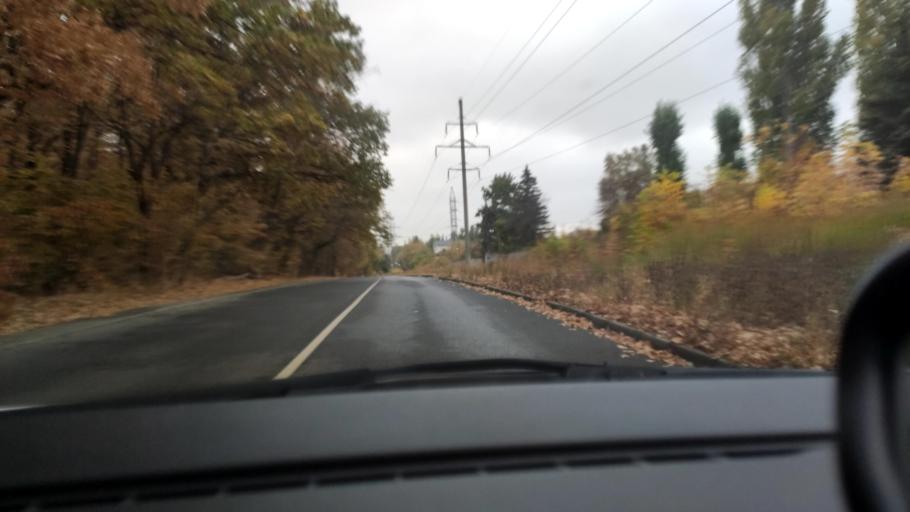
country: RU
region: Voronezj
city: Voronezh
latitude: 51.7168
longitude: 39.2345
